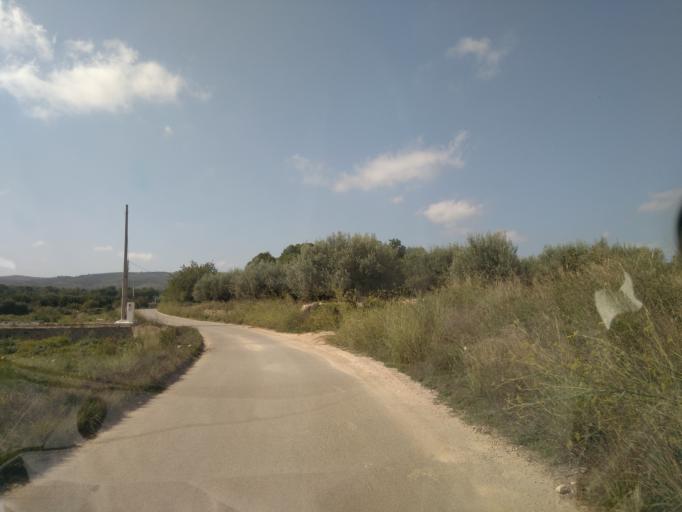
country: ES
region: Valencia
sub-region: Provincia de Valencia
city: Tous
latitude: 39.1692
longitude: -0.5859
